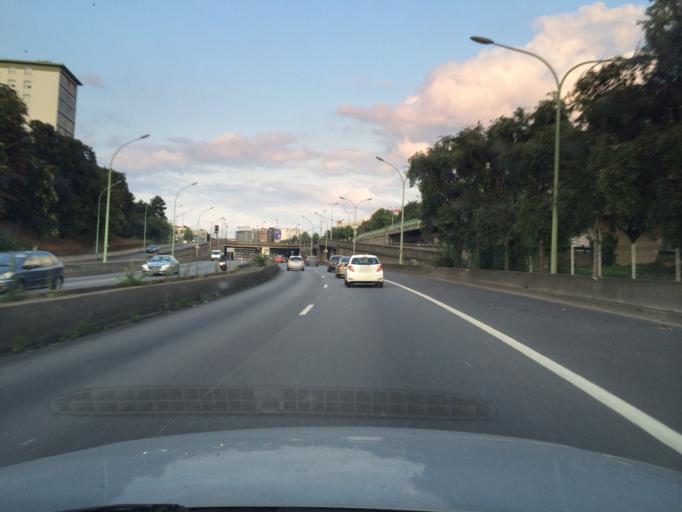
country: FR
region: Ile-de-France
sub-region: Departement du Val-de-Marne
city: Le Kremlin-Bicetre
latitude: 48.8164
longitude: 2.3564
